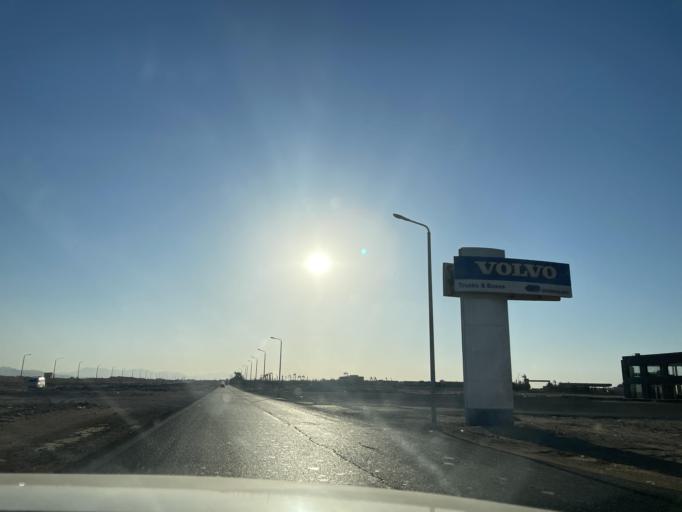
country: EG
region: Red Sea
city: Hurghada
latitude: 27.2173
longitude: 33.7994
